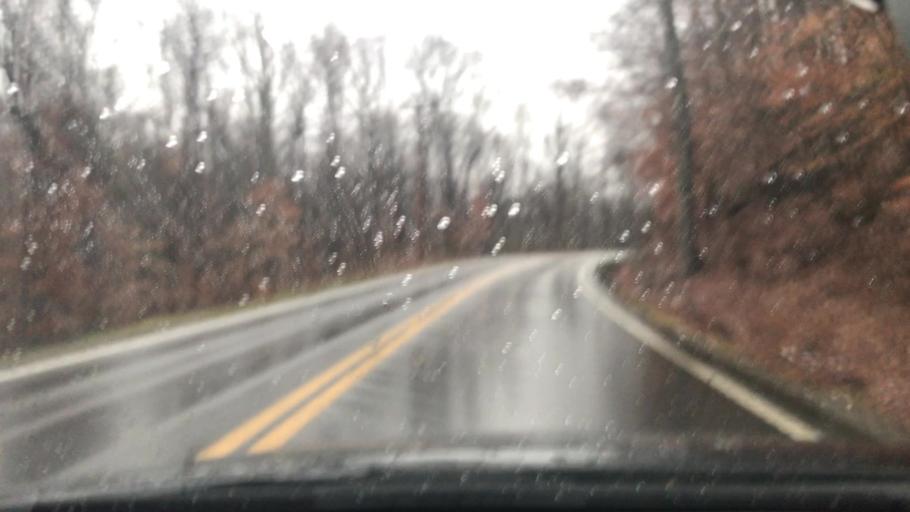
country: US
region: Tennessee
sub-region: Cheatham County
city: Ashland City
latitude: 36.2766
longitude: -87.1255
